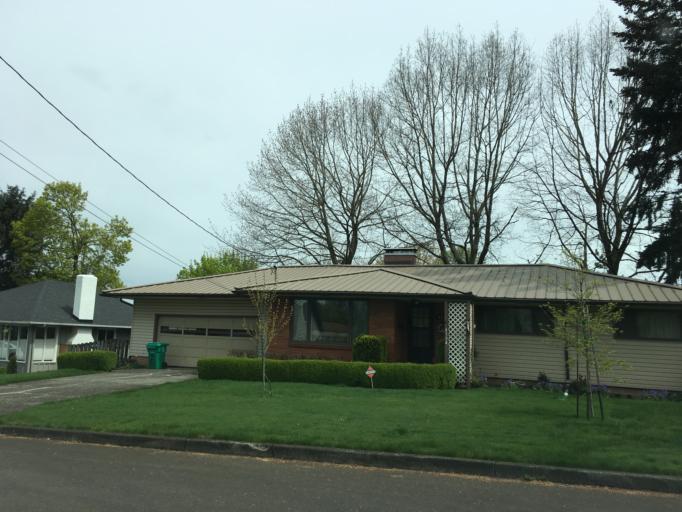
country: US
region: Oregon
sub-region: Multnomah County
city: Lents
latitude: 45.5540
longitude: -122.5766
